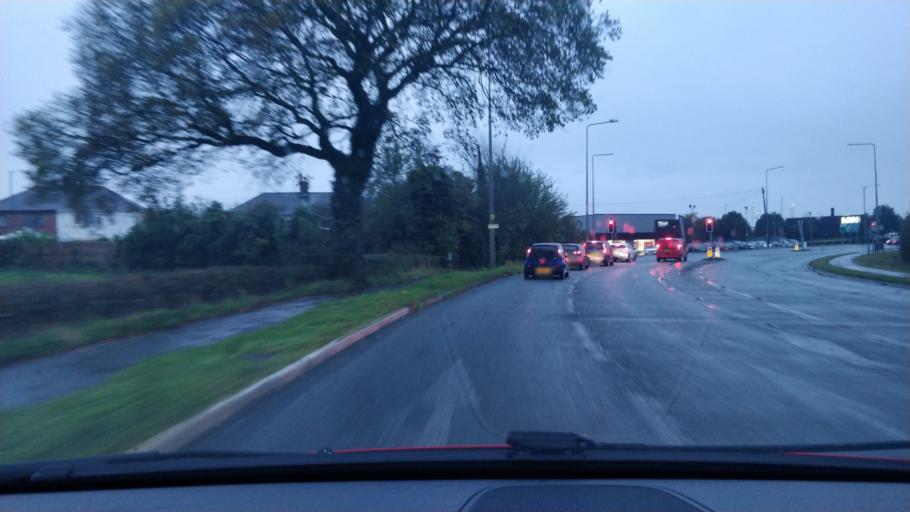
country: GB
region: England
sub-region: Lancashire
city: Poulton le Fylde
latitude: 53.7880
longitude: -2.9782
